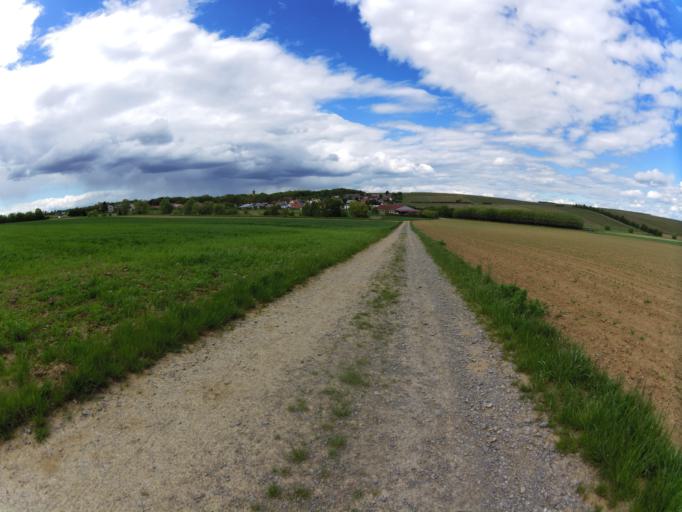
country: DE
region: Bavaria
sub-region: Regierungsbezirk Unterfranken
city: Volkach
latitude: 49.8845
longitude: 10.2327
